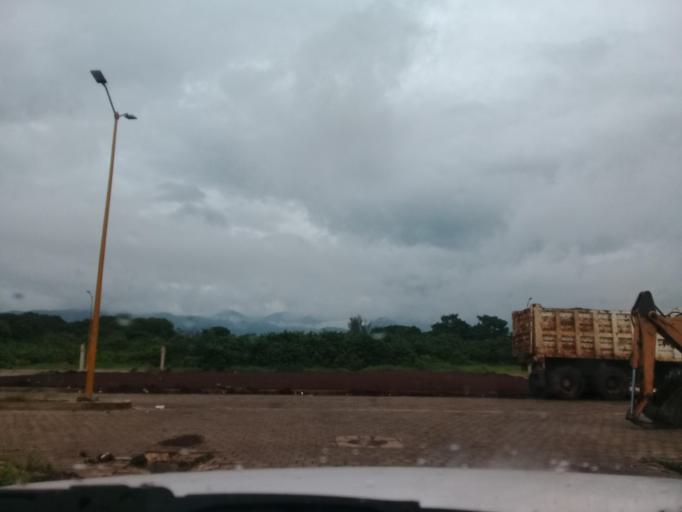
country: MX
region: Veracruz
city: San Andres Tuxtla
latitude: 18.4268
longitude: -95.2176
